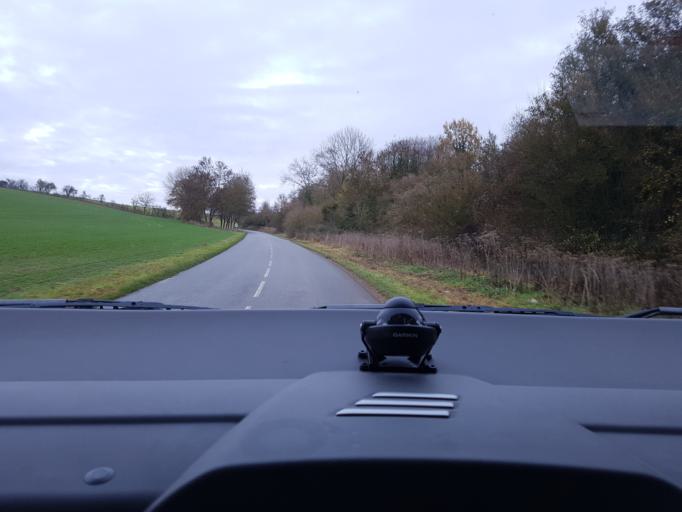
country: FR
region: Picardie
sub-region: Departement de l'Oise
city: Songeons
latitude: 49.5698
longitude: 1.8604
